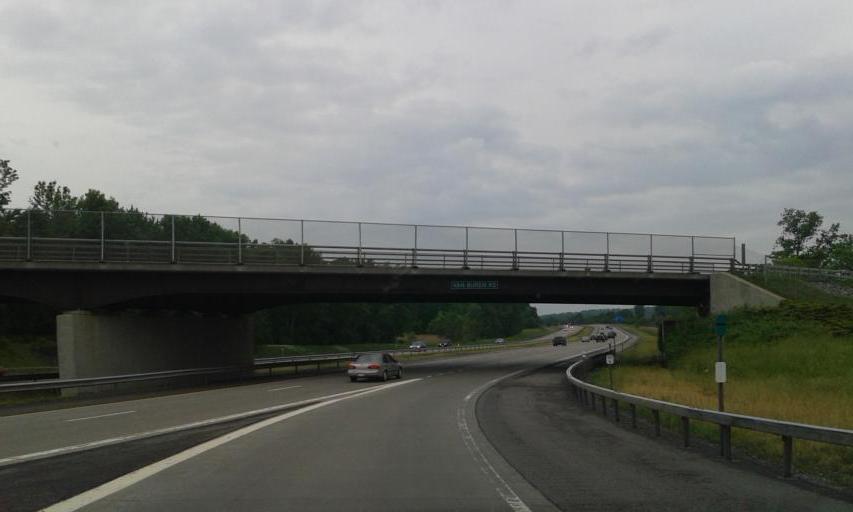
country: US
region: New York
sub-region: Onondaga County
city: Seneca Knolls
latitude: 43.1074
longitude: -76.2883
